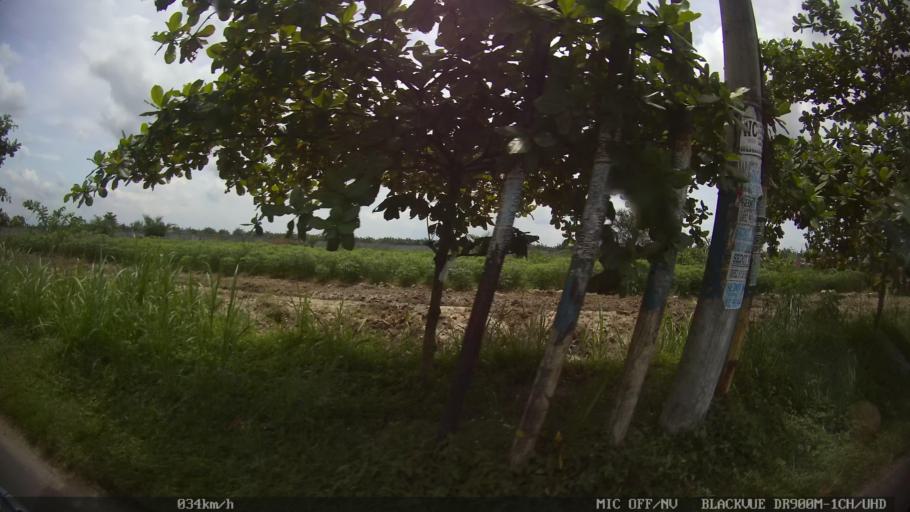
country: ID
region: North Sumatra
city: Percut
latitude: 3.5828
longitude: 98.8832
